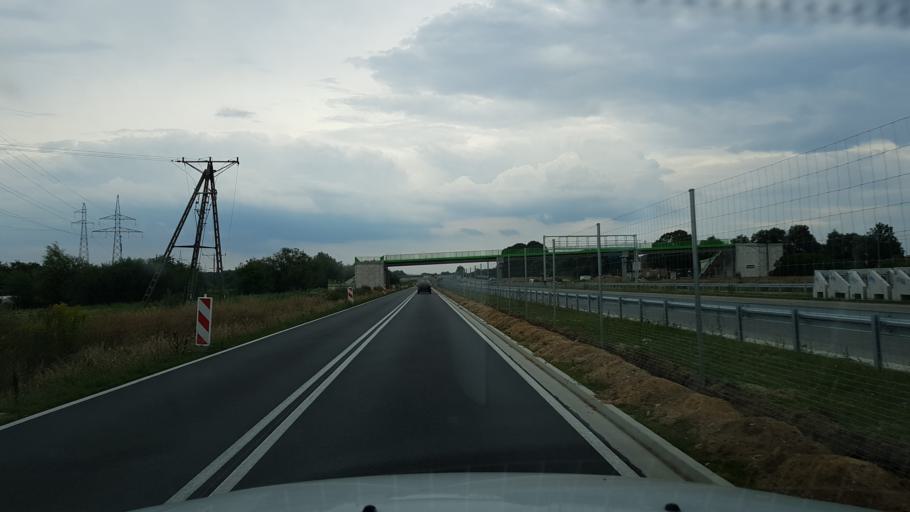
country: PL
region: West Pomeranian Voivodeship
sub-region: Powiat szczecinecki
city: Szczecinek
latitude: 53.7199
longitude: 16.6949
